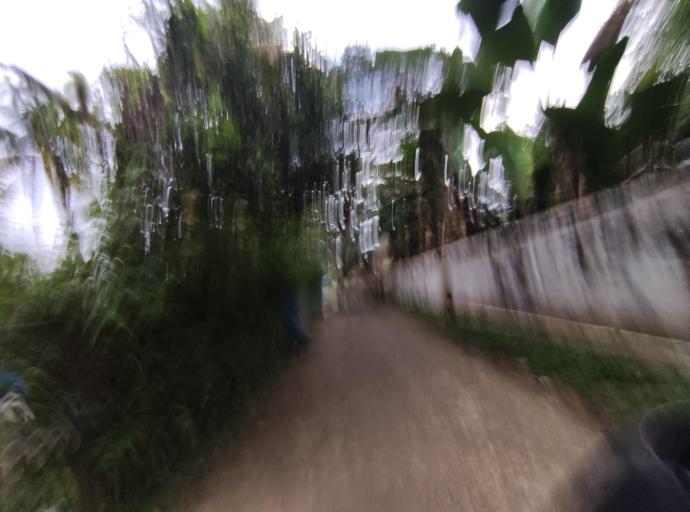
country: IN
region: Kerala
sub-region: Alappuzha
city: Shertallai
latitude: 9.6290
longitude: 76.4285
